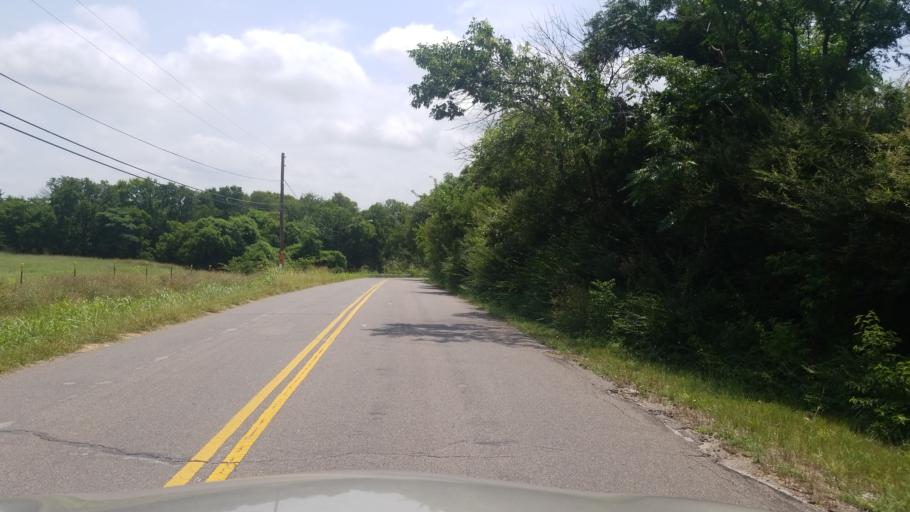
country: US
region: Texas
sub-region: Dallas County
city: Duncanville
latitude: 32.6863
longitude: -96.9353
